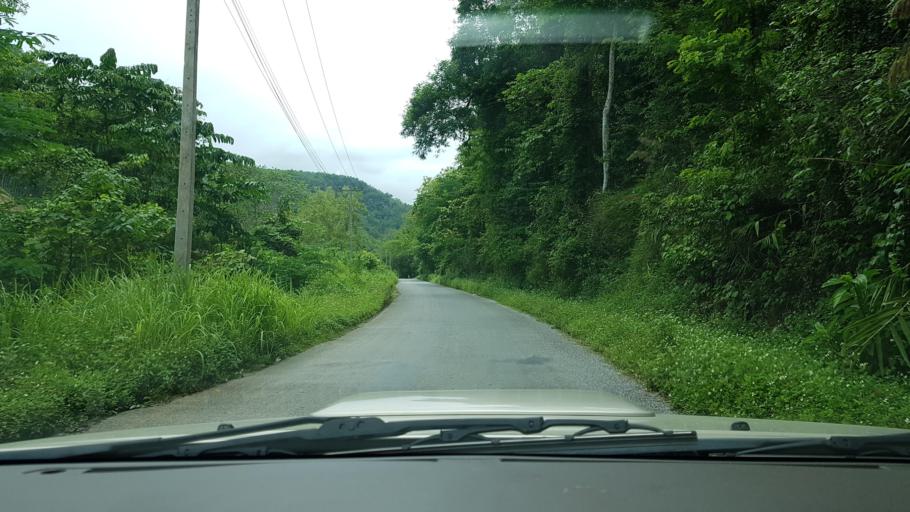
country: LA
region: Phongsali
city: Khoa
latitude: 21.0498
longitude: 102.4120
